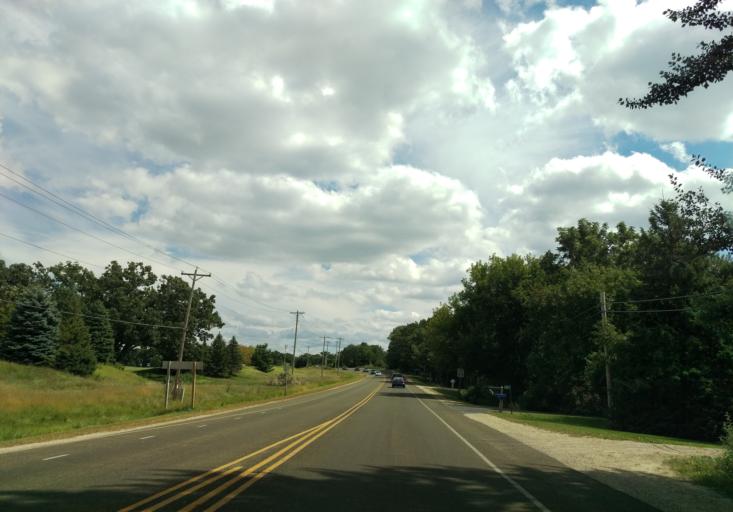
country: US
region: Wisconsin
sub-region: Dane County
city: Shorewood Hills
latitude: 43.1119
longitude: -89.4628
